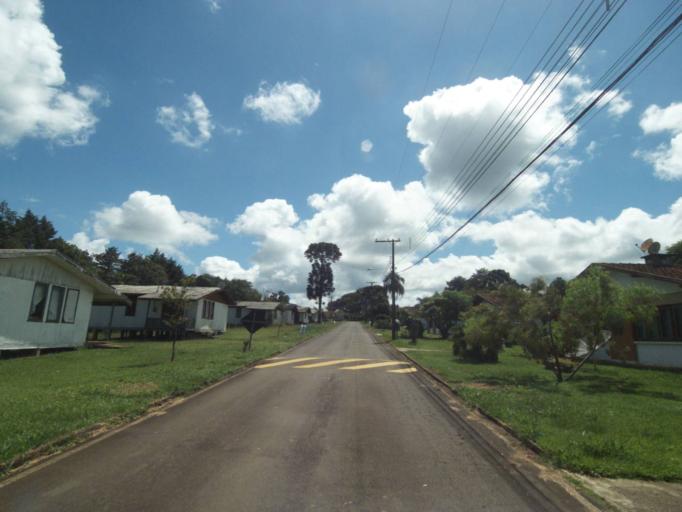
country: BR
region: Parana
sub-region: Chopinzinho
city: Chopinzinho
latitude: -25.7951
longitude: -52.0907
